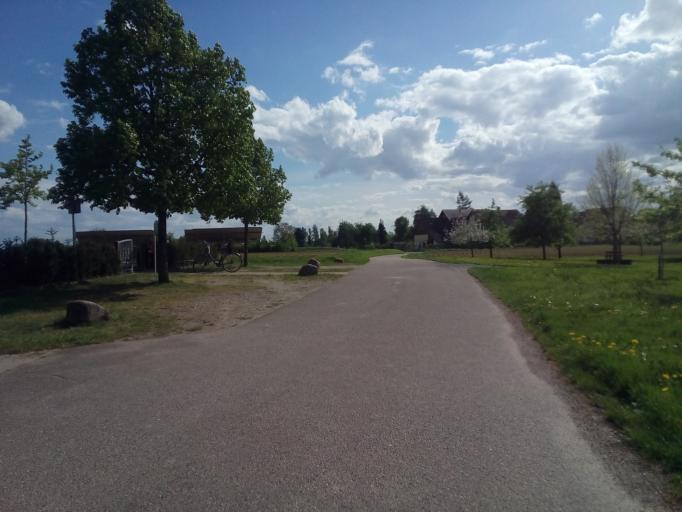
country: DE
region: Baden-Wuerttemberg
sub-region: Karlsruhe Region
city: Lichtenau
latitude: 48.6955
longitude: 7.9917
